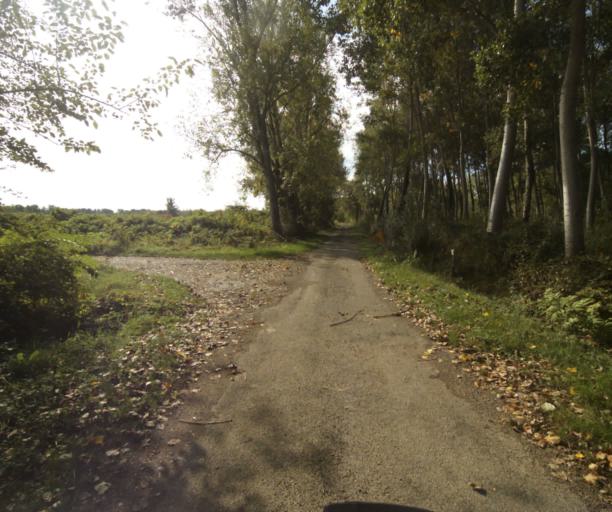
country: FR
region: Midi-Pyrenees
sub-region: Departement du Tarn-et-Garonne
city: Finhan
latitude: 43.8956
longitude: 1.2102
